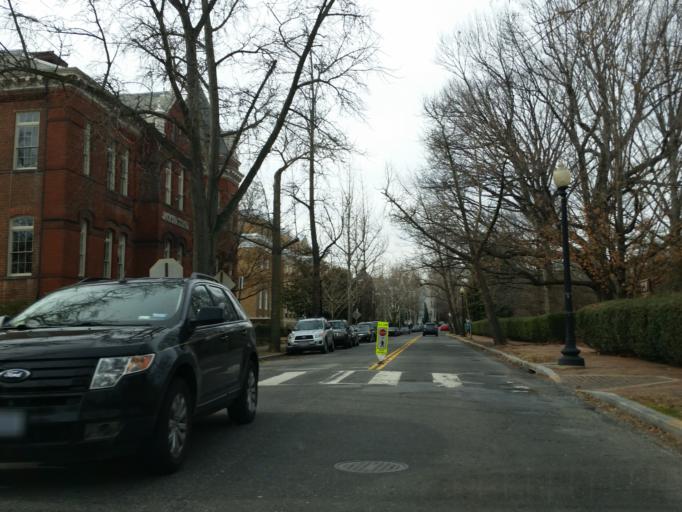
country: US
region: Washington, D.C.
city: Washington, D.C.
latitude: 38.9128
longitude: -77.0608
